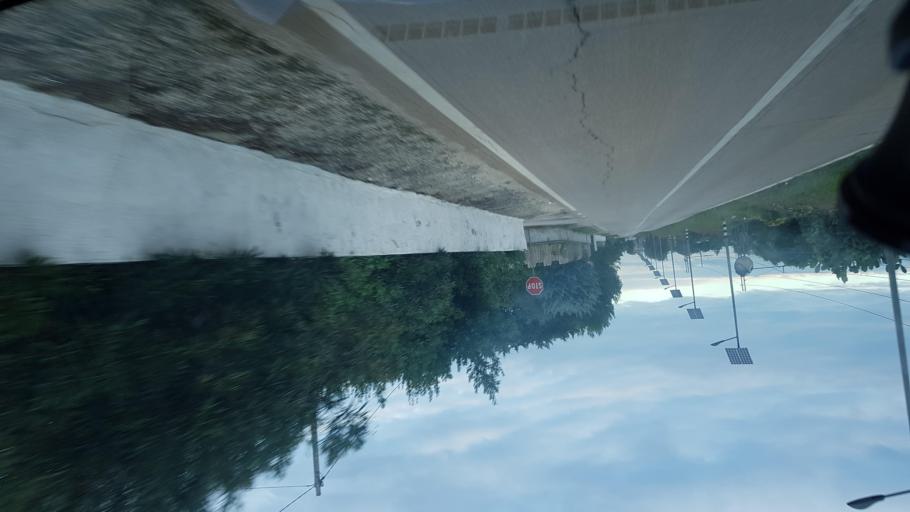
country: IT
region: Apulia
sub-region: Provincia di Brindisi
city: Latiano
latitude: 40.5413
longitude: 17.6962
